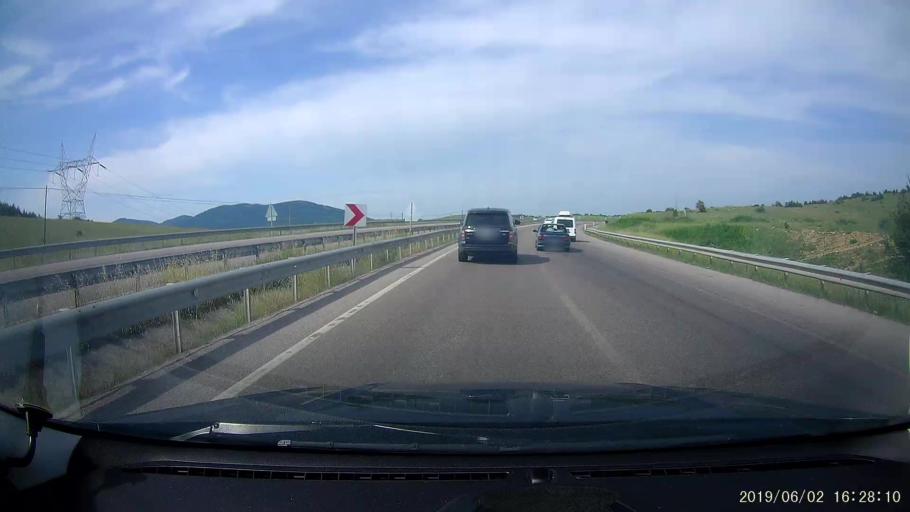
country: TR
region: Samsun
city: Ladik
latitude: 41.0059
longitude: 35.8416
